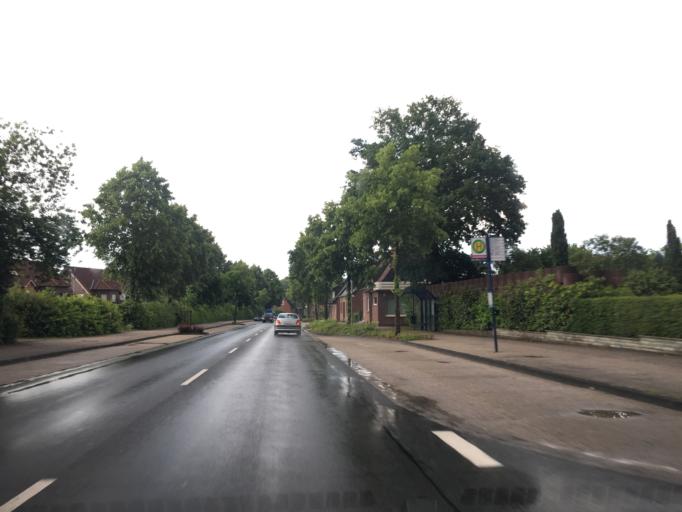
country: DE
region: North Rhine-Westphalia
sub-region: Regierungsbezirk Munster
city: Nordwalde
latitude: 52.0823
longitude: 7.4693
